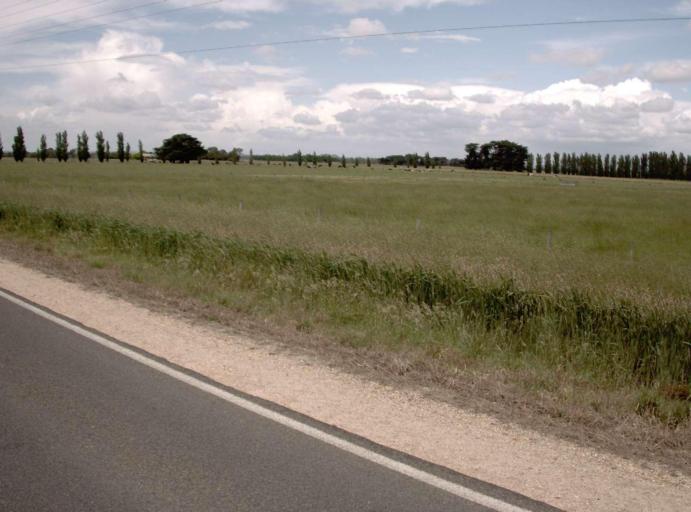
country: AU
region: Victoria
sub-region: Wellington
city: Sale
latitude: -38.0168
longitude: 147.0091
